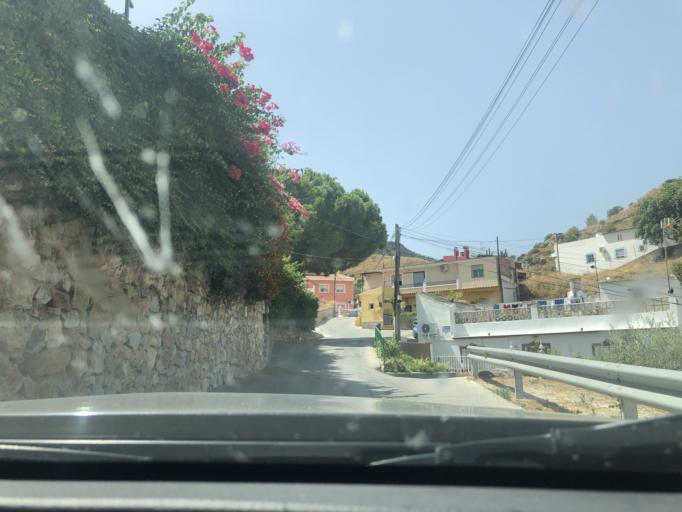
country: ES
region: Andalusia
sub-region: Provincia de Malaga
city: Cartama
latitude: 36.7103
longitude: -4.6260
